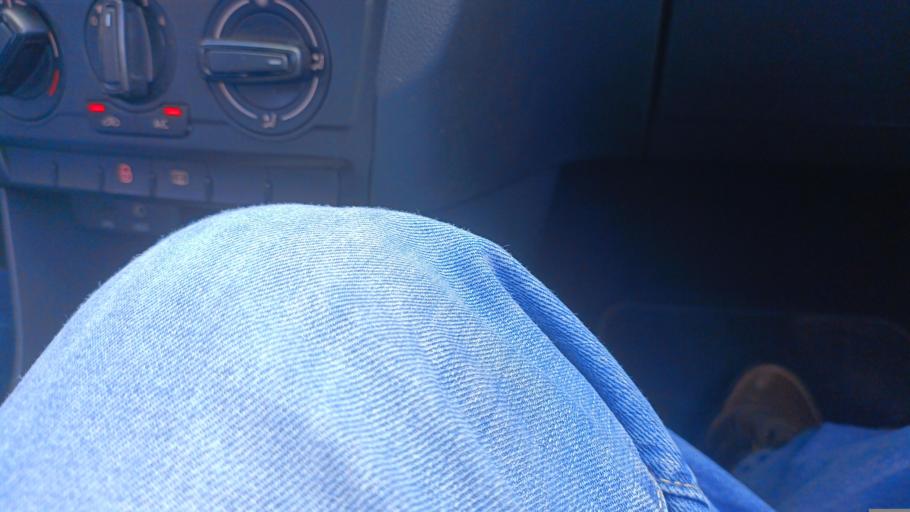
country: MX
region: Guanajuato
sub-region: San Luis de la Paz
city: San Luis de la Paz
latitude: 21.2903
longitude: -100.4911
